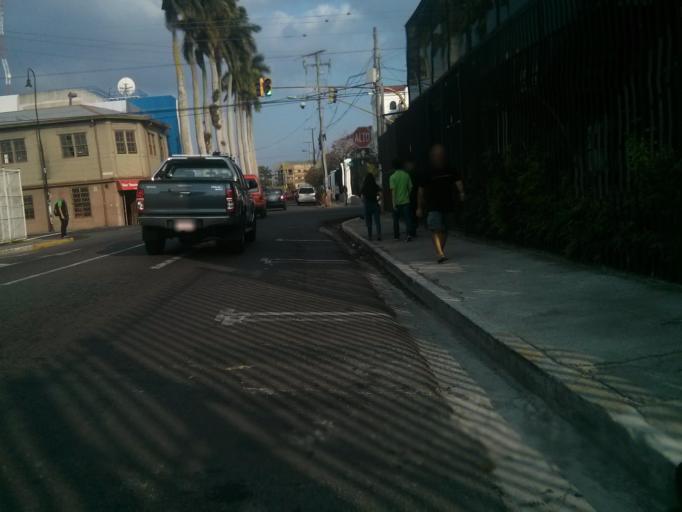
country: CR
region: San Jose
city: Calle Blancos
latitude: 9.9368
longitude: -84.0672
